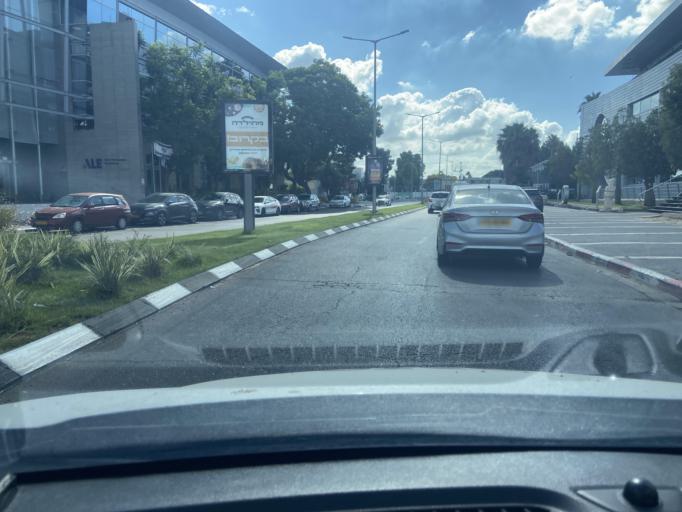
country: IL
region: Central District
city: Yehud
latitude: 32.0279
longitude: 34.8971
